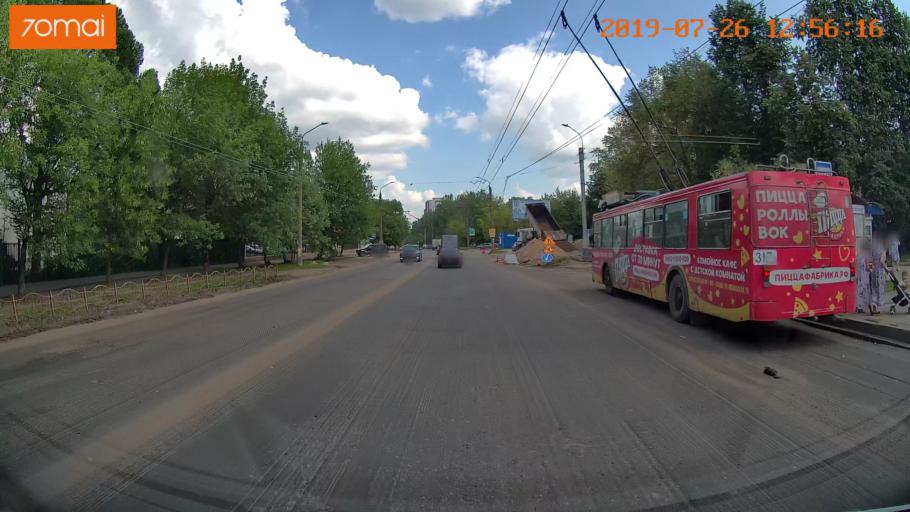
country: RU
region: Ivanovo
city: Bogorodskoye
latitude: 57.0165
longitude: 41.0094
